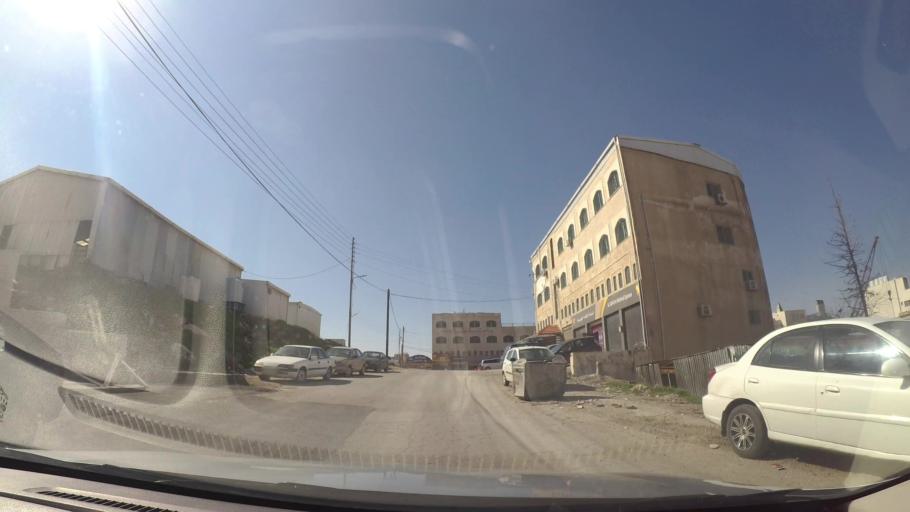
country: JO
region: Amman
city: Al Bunayyat ash Shamaliyah
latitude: 31.9154
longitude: 35.9090
